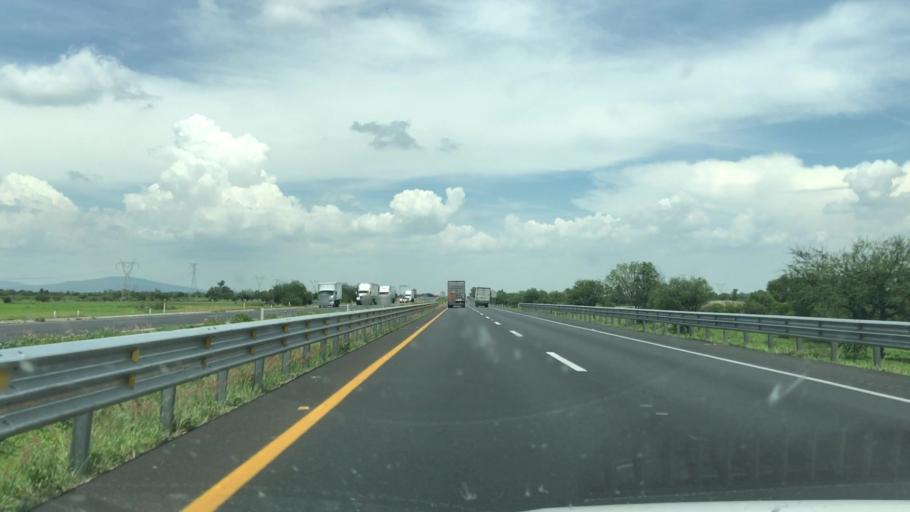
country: MX
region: Guanajuato
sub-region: Villagran
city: Los Angeles
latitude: 20.5722
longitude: -100.9096
